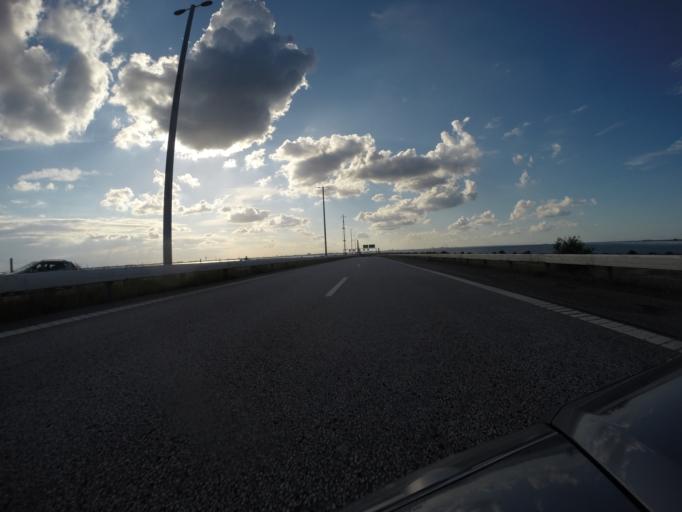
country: DK
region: Capital Region
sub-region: Dragor Kommune
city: Dragor
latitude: 55.6066
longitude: 12.7376
